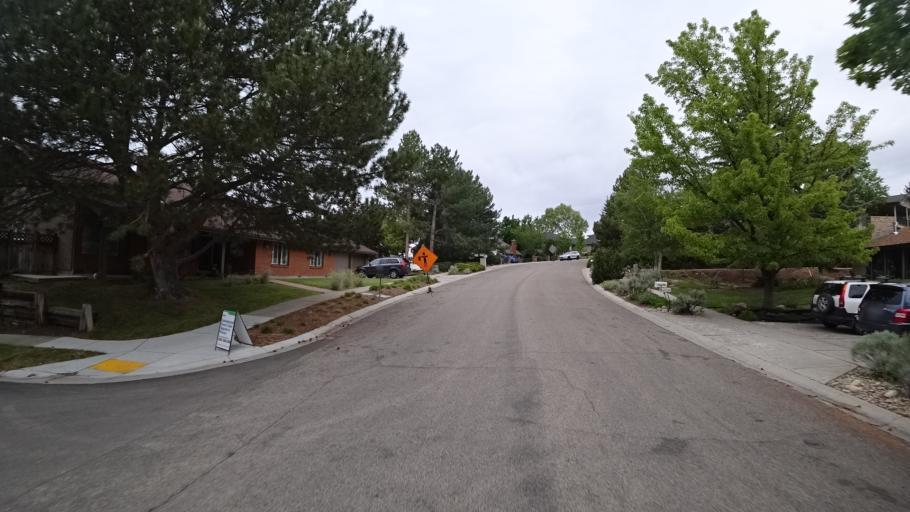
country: US
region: Idaho
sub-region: Ada County
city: Boise
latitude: 43.6148
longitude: -116.1717
